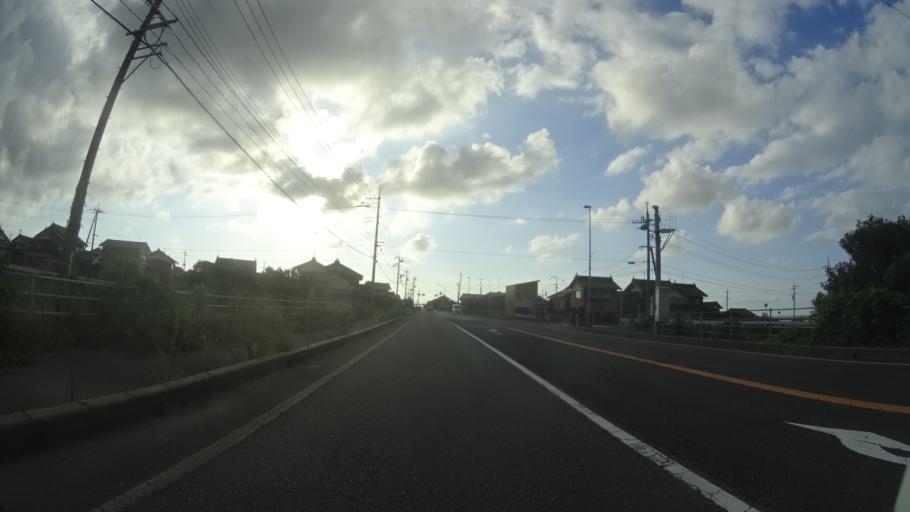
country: JP
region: Tottori
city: Kurayoshi
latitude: 35.5235
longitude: 133.5927
